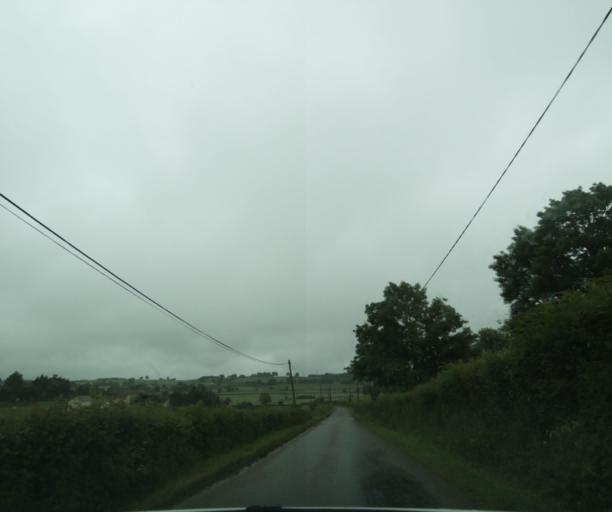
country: FR
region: Bourgogne
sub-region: Departement de Saone-et-Loire
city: Charolles
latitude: 46.4688
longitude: 4.2346
